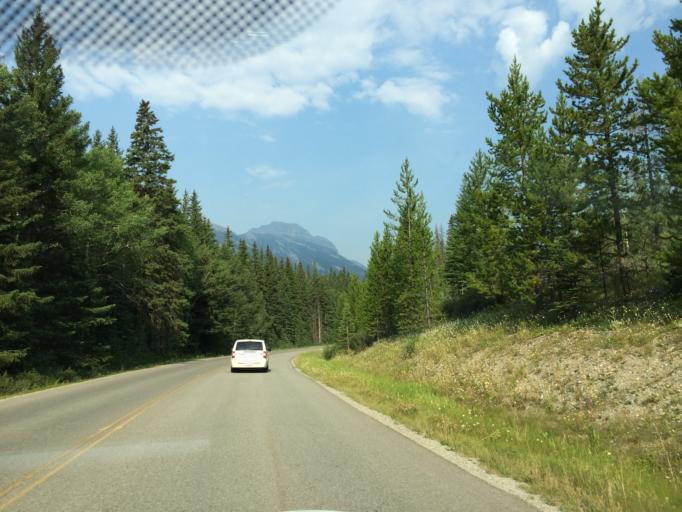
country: CA
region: Alberta
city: Banff
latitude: 51.1720
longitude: -115.7056
